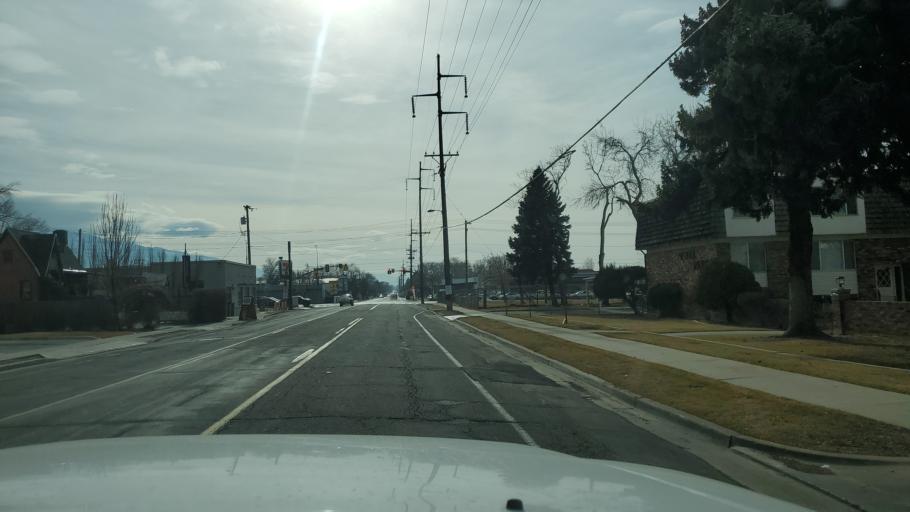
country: US
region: Utah
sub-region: Salt Lake County
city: Millcreek
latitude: 40.7011
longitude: -111.8656
